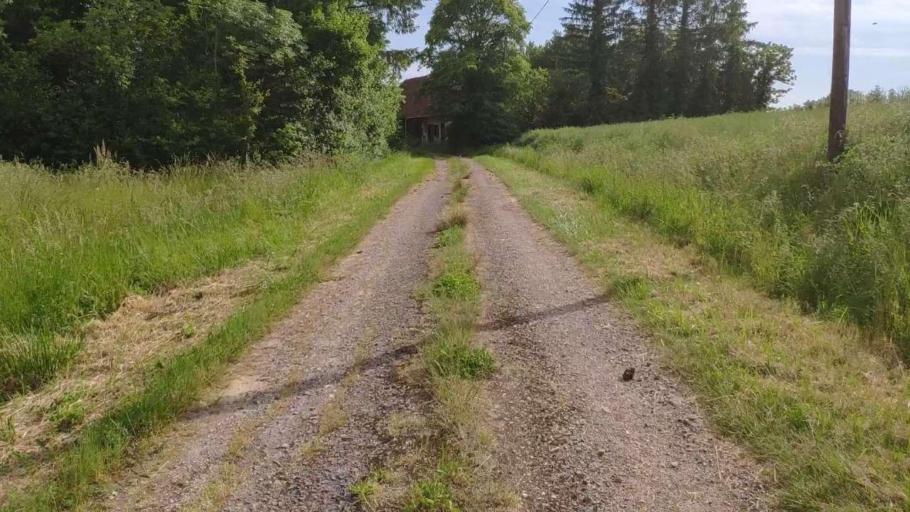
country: FR
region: Bourgogne
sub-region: Departement de Saone-et-Loire
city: Saint-Germain-du-Bois
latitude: 46.8142
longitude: 5.3391
